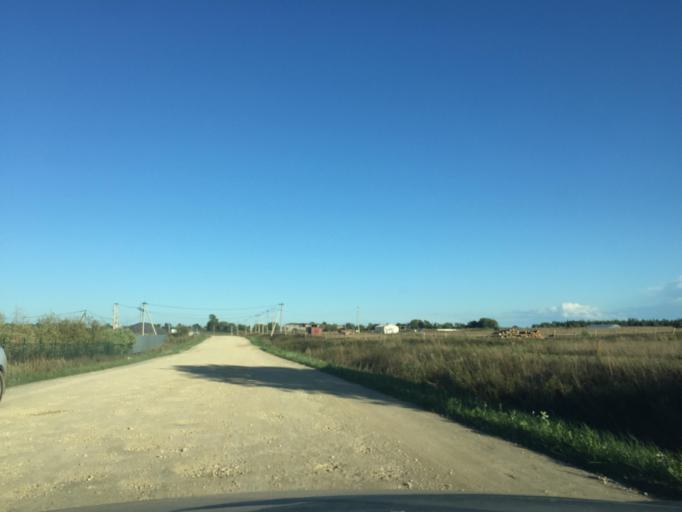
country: RU
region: Leningrad
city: Siverskiy
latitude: 59.3310
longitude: 30.0183
